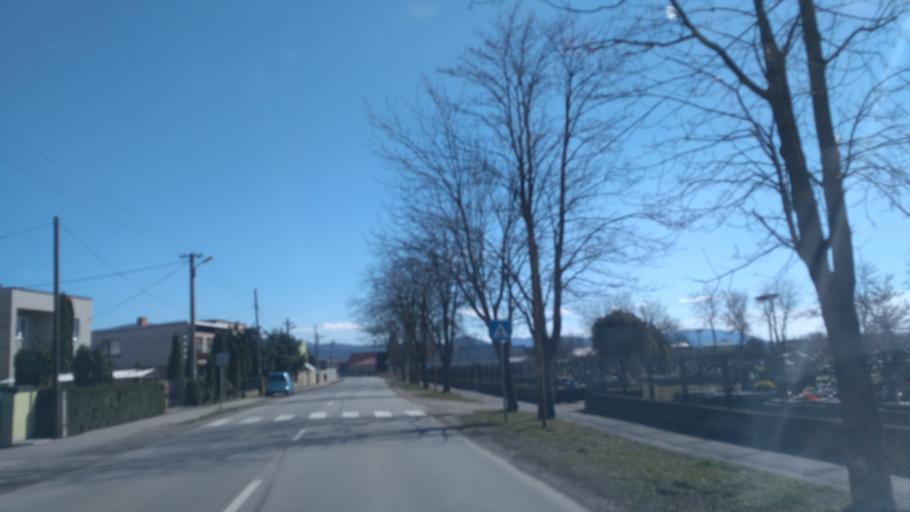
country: SK
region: Kosicky
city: Kosice
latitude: 48.6100
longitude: 21.3206
